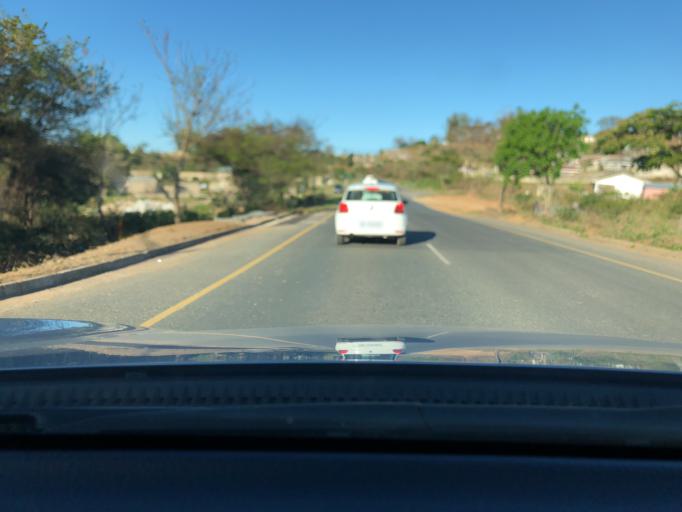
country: ZA
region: KwaZulu-Natal
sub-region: eThekwini Metropolitan Municipality
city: Umkomaas
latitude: -30.0358
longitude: 30.8181
